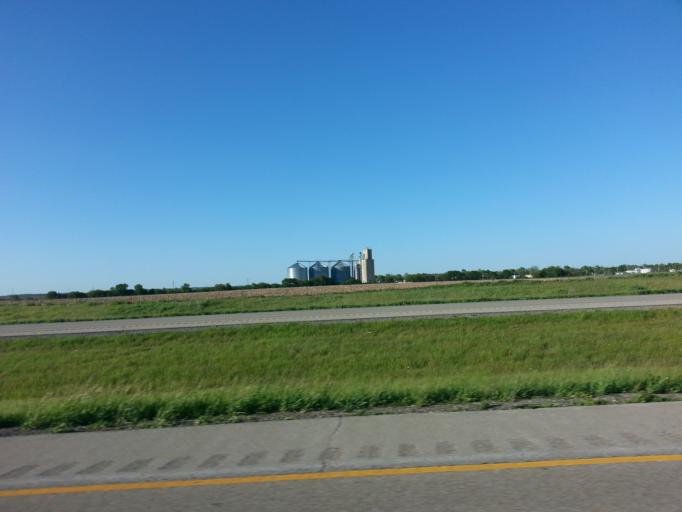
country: US
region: Illinois
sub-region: McLean County
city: Le Roy
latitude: 40.3443
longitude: -88.7774
